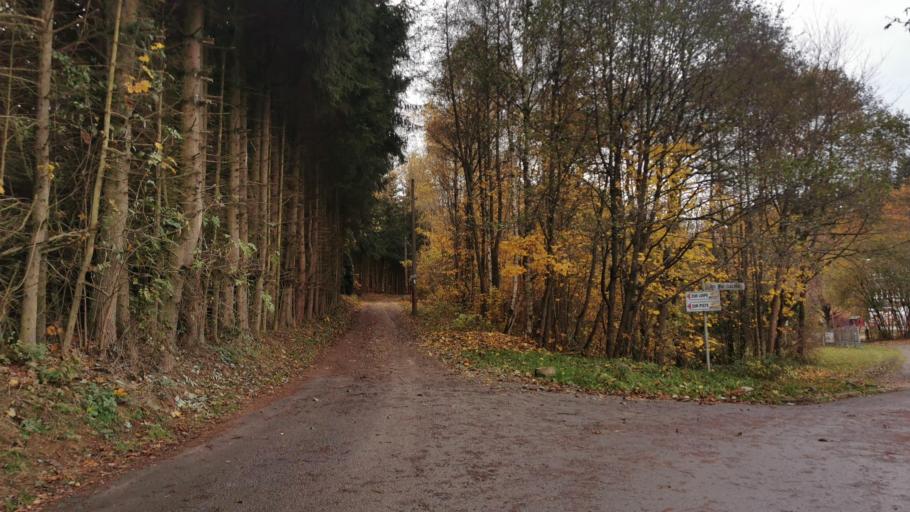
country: DE
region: Thuringia
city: Wurzbach
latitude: 50.4636
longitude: 11.5303
